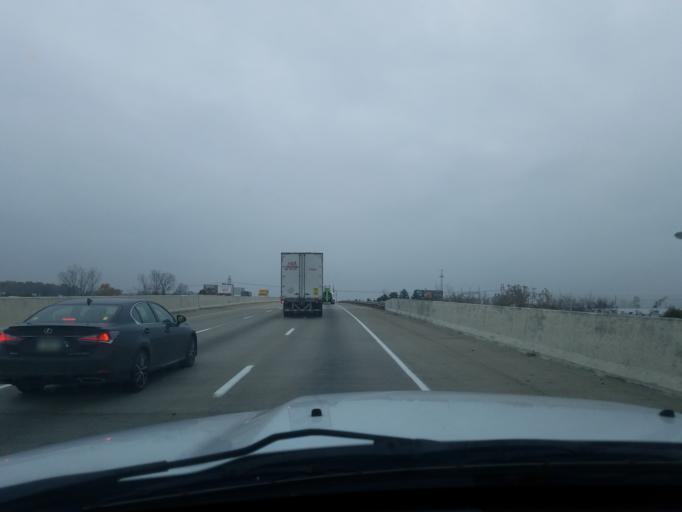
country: US
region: Indiana
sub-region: Marion County
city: Beech Grove
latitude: 39.7106
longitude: -86.0586
